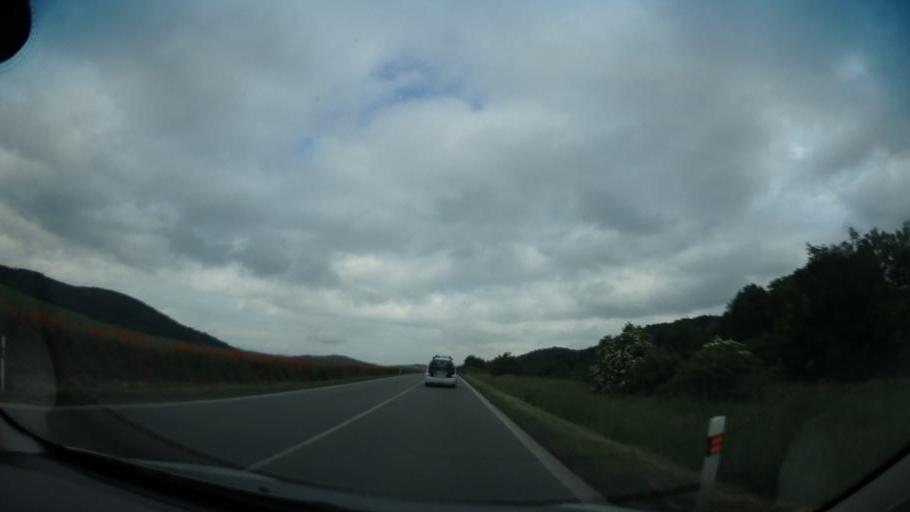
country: CZ
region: South Moravian
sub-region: Okres Brno-Venkov
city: Lelekovice
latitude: 49.2933
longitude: 16.5561
